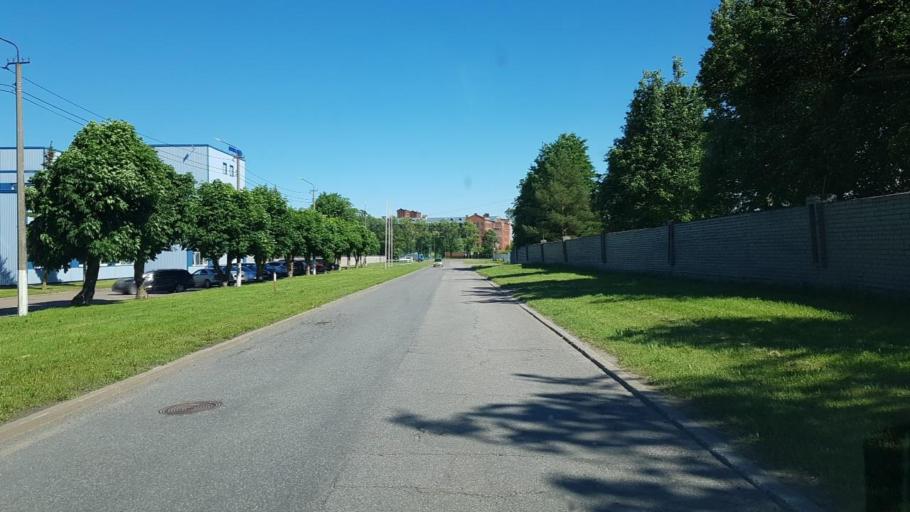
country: EE
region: Ida-Virumaa
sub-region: Narva linn
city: Narva
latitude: 59.3596
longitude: 28.1824
